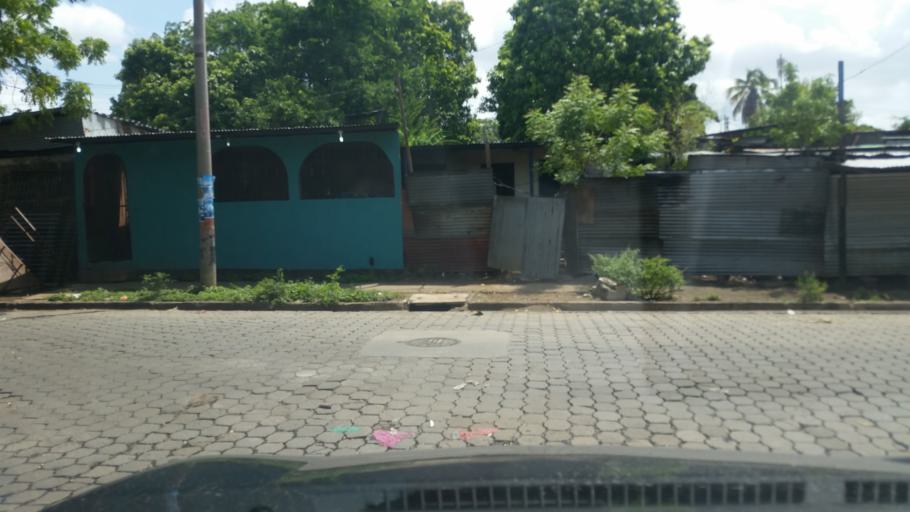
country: NI
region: Managua
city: Managua
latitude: 12.1119
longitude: -86.2337
